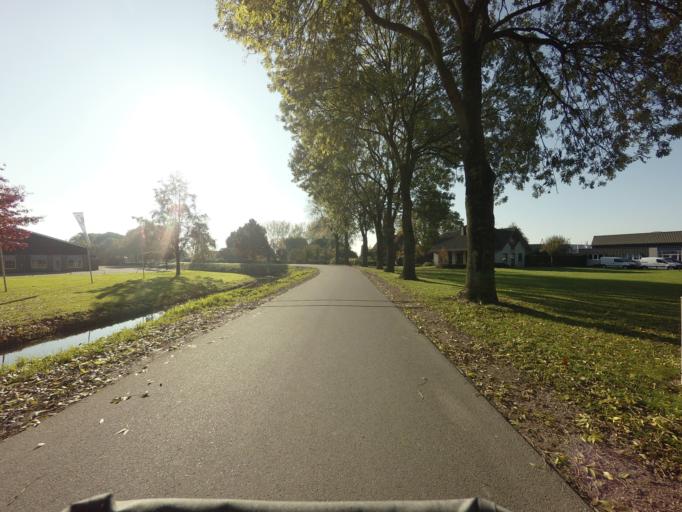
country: NL
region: North Brabant
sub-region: Gemeente Woudrichem
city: Almkerk
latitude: 51.7281
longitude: 4.9620
